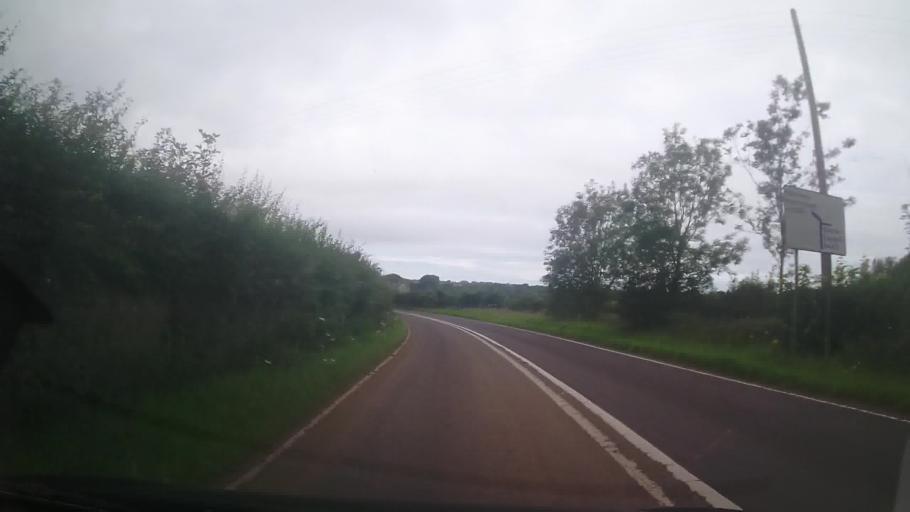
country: GB
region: Wales
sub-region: Gwynedd
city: Caernarfon
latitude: 53.1752
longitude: -4.3048
